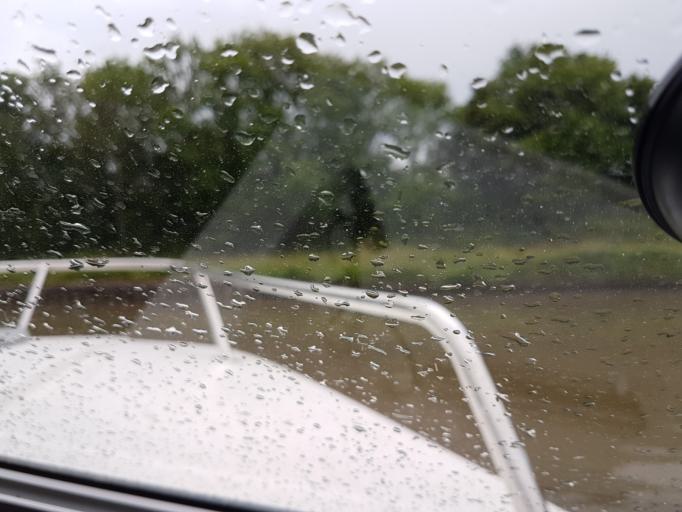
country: FR
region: Bourgogne
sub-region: Departement de la Nievre
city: Corbigny
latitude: 47.3609
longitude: 3.6194
